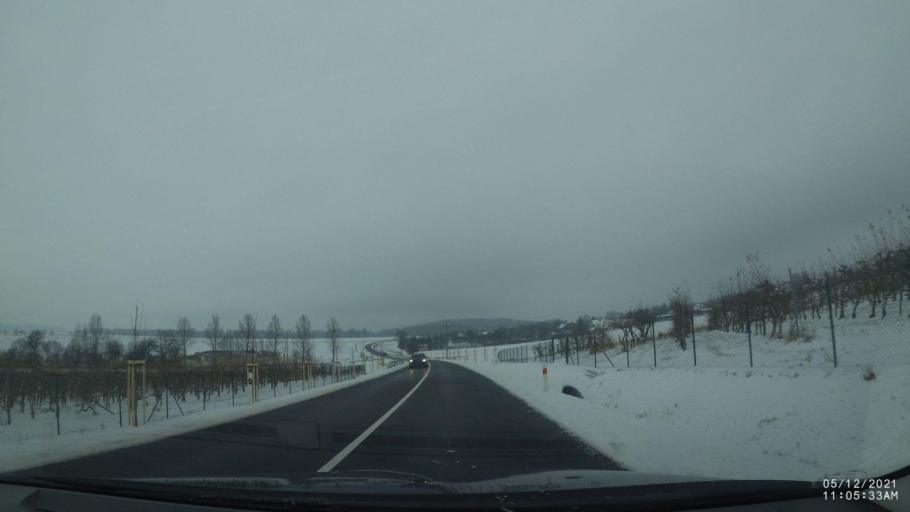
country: CZ
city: Solnice
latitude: 50.1751
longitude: 16.2220
